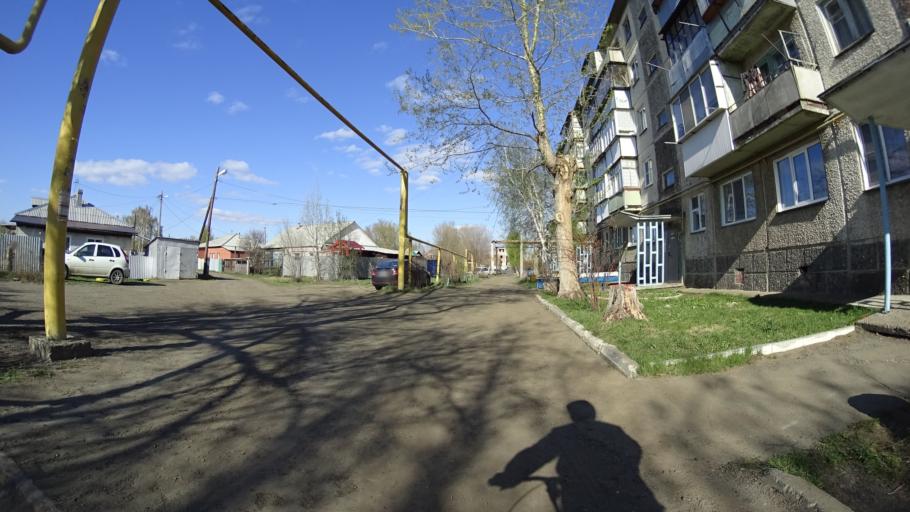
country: RU
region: Chelyabinsk
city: Troitsk
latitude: 54.1053
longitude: 61.5567
